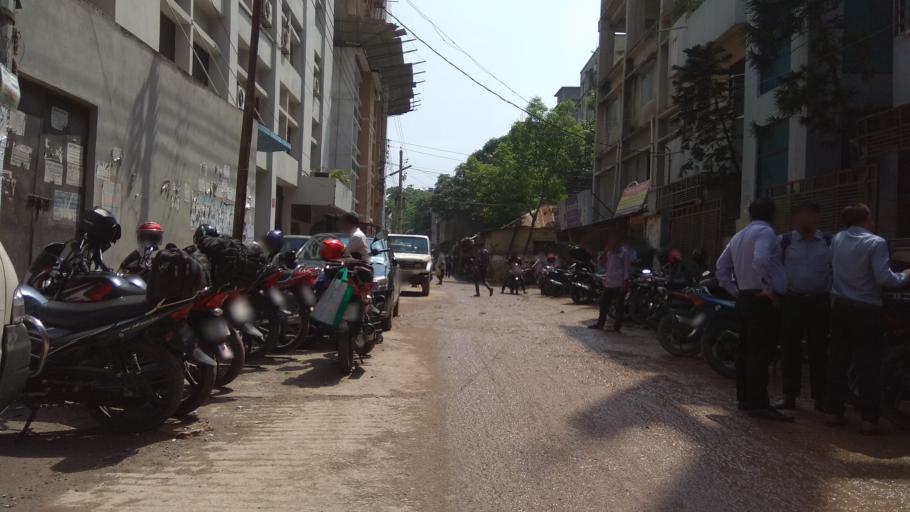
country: BD
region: Dhaka
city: Azimpur
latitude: 23.8032
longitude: 90.3620
